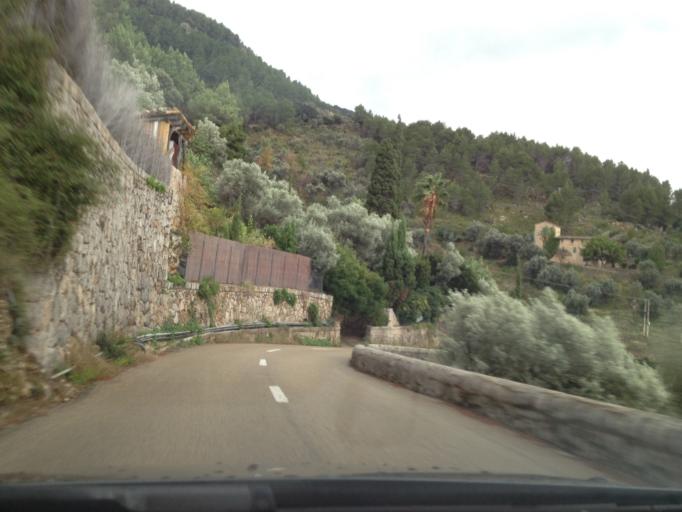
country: ES
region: Balearic Islands
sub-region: Illes Balears
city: Deia
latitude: 39.7715
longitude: 2.6684
